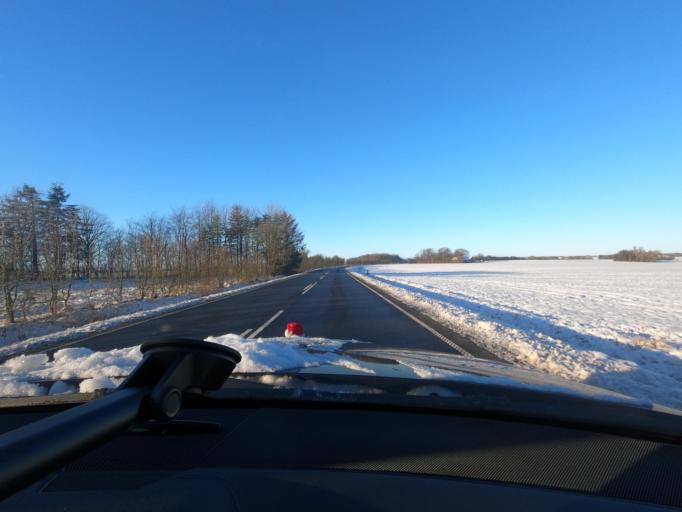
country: DK
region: South Denmark
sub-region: Tonder Kommune
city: Toftlund
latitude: 55.1603
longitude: 9.0828
